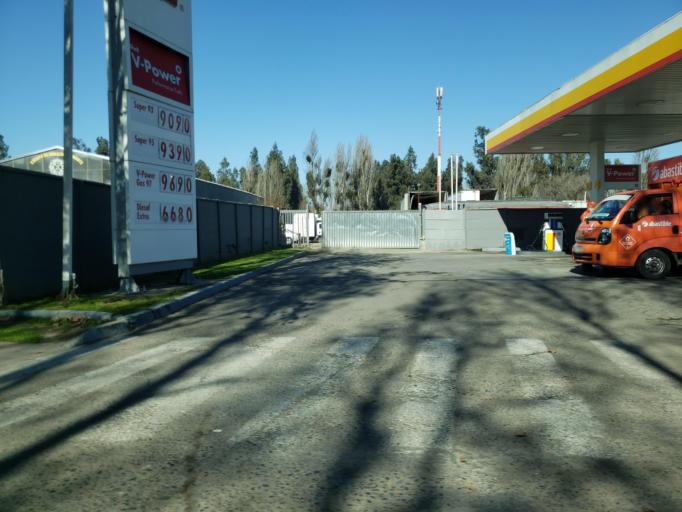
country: CL
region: Santiago Metropolitan
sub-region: Provincia de Talagante
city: El Monte
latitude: -33.6814
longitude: -70.9822
